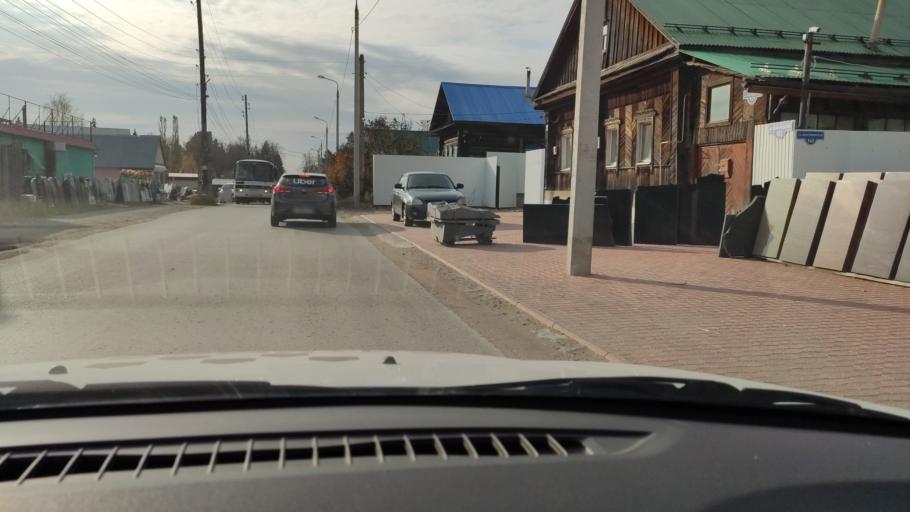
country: RU
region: Perm
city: Kondratovo
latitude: 58.0567
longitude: 56.1232
